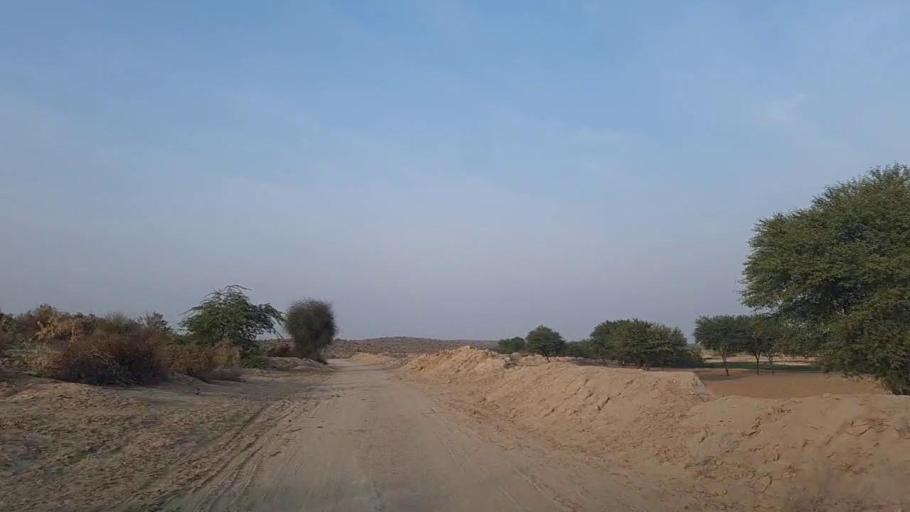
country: PK
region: Sindh
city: Jam Sahib
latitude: 26.4088
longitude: 68.6005
